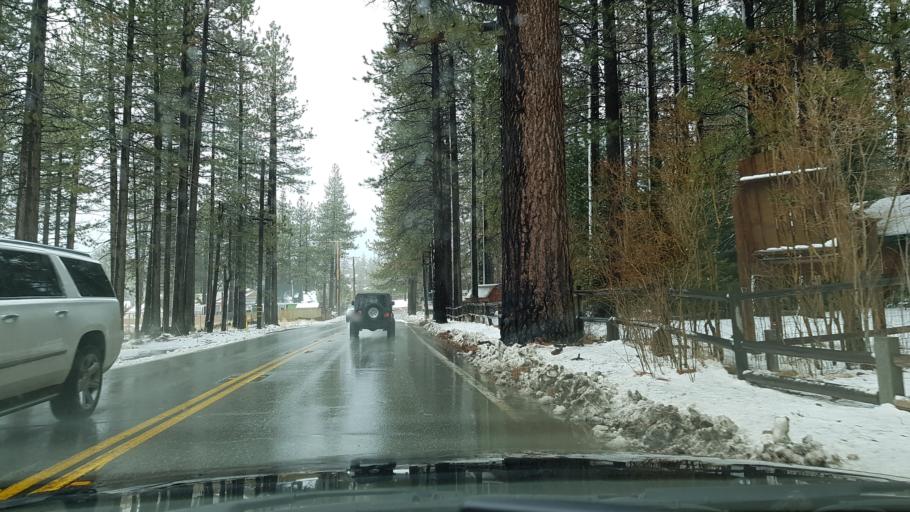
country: US
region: California
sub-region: San Bernardino County
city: Big Bear Lake
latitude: 34.2651
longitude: -116.9385
